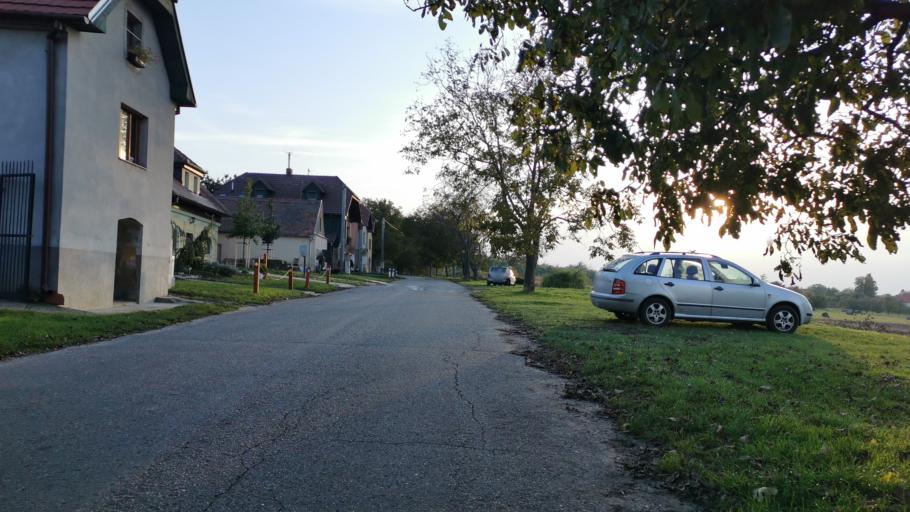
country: SK
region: Trnavsky
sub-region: Okres Skalica
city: Skalica
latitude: 48.8376
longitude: 17.2421
